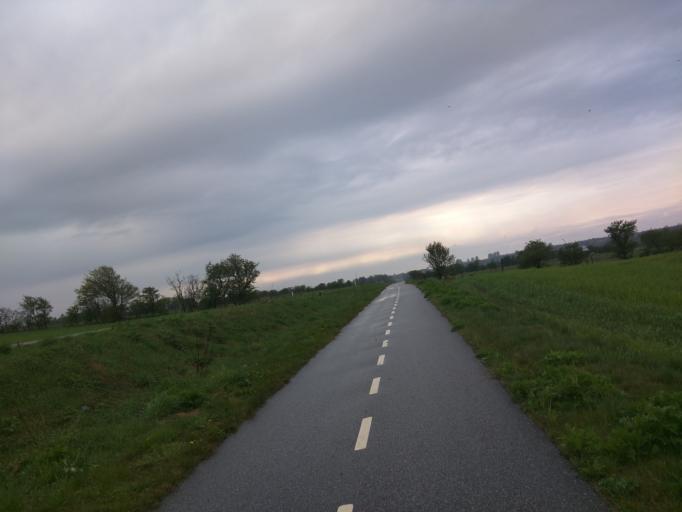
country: DK
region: Central Jutland
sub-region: Viborg Kommune
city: Viborg
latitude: 56.4619
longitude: 9.4854
